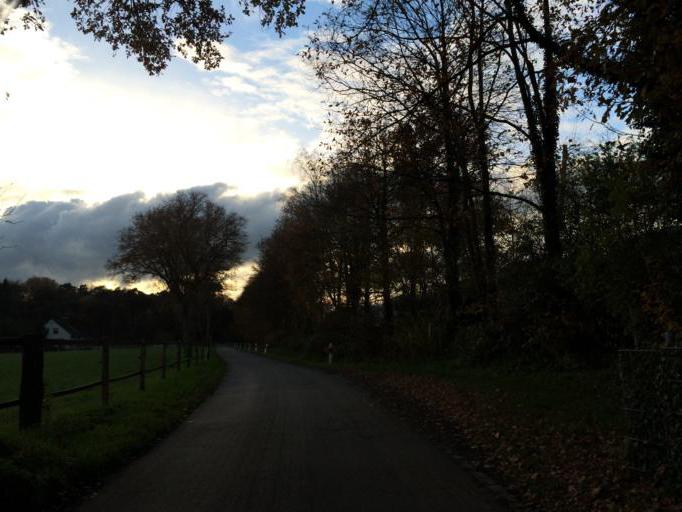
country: DE
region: North Rhine-Westphalia
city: Marl
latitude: 51.6742
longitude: 7.0424
